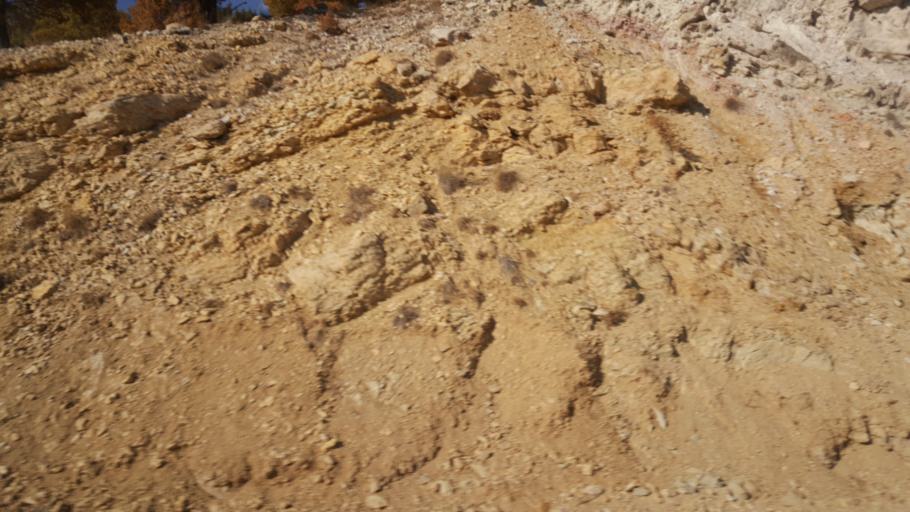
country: TR
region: Eskisehir
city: Kirka
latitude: 39.3245
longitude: 30.5693
